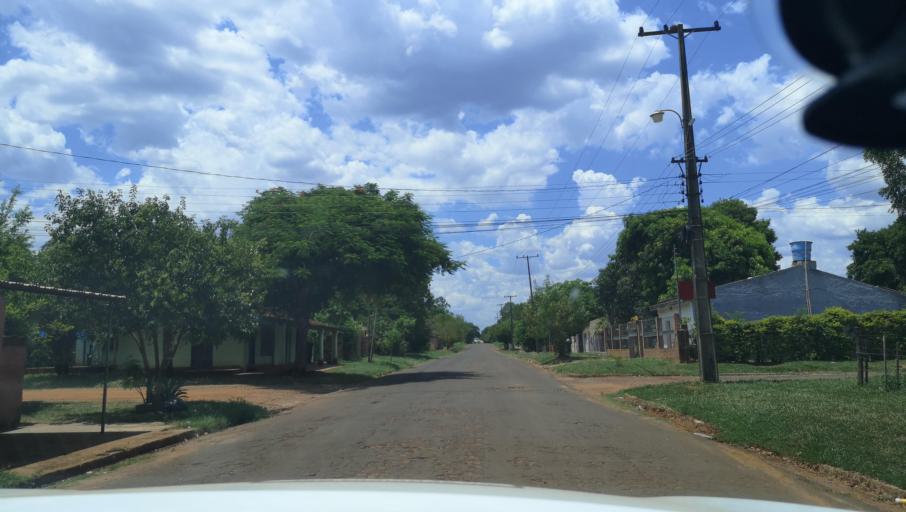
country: PY
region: Itapua
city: Carmen del Parana
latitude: -27.1692
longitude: -56.2454
